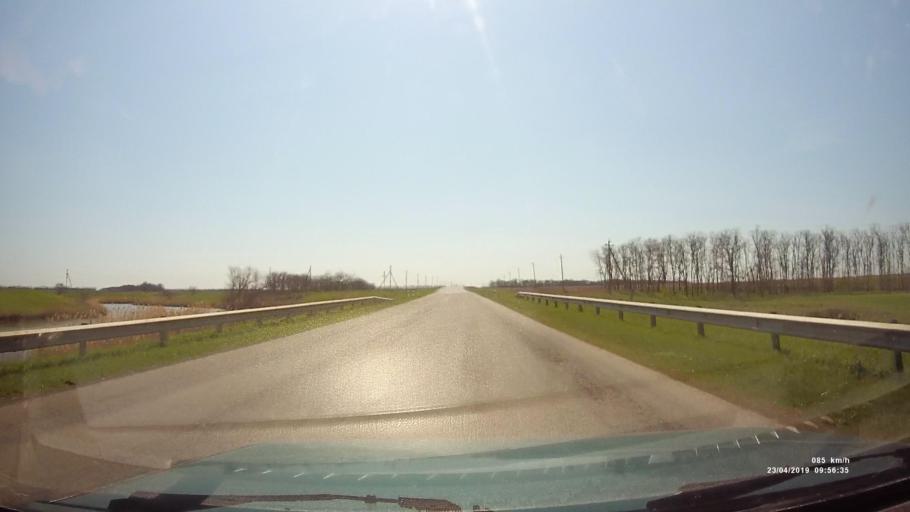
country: RU
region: Rostov
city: Orlovskiy
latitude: 46.7968
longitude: 42.0737
